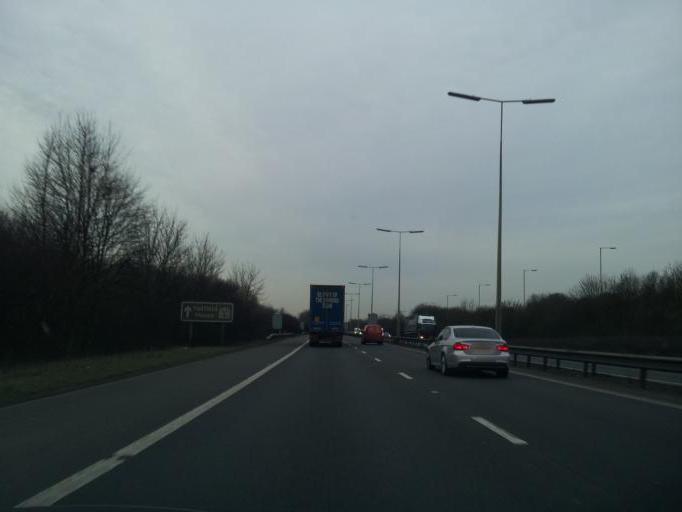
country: GB
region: England
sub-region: Hertfordshire
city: Hatfield
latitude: 51.7410
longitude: -0.2396
